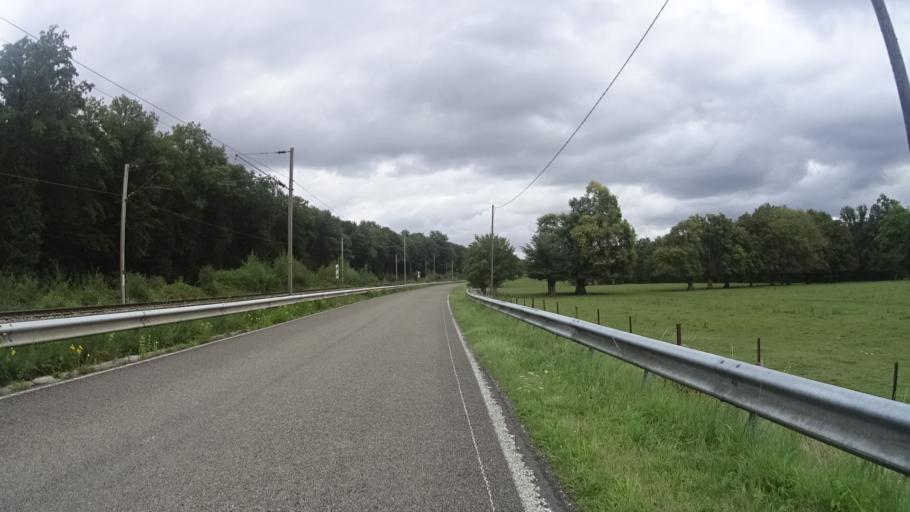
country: FR
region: Nord-Pas-de-Calais
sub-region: Departement du Nord
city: Maroilles
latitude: 50.1707
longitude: 3.7745
